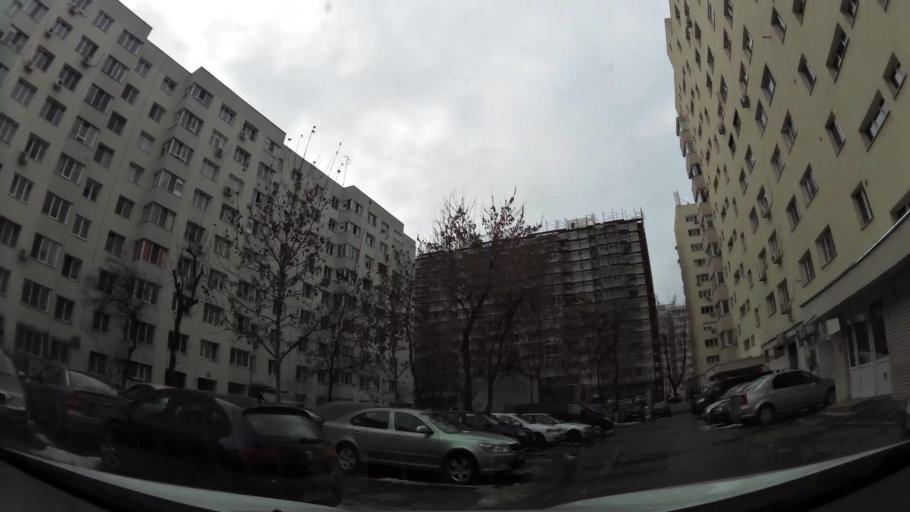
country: RO
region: Ilfov
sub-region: Comuna Popesti-Leordeni
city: Popesti-Leordeni
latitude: 44.4122
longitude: 26.1650
